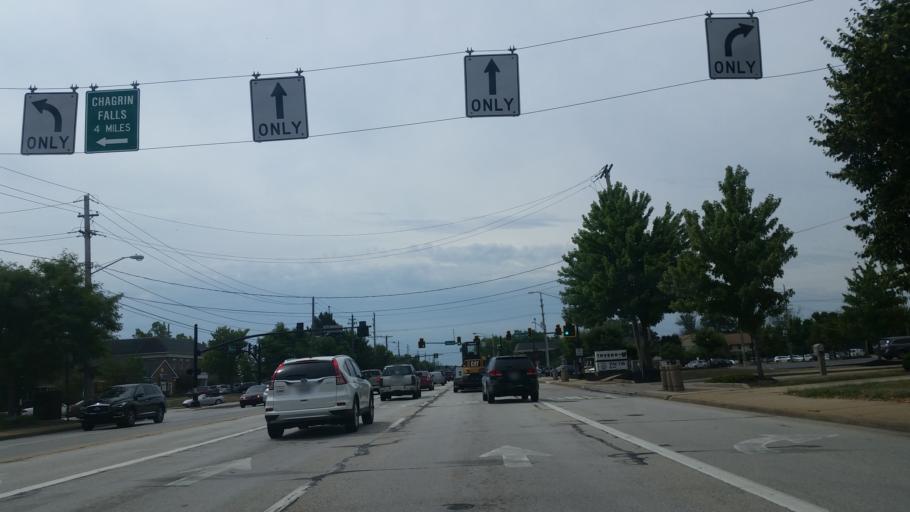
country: US
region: Ohio
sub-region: Cuyahoga County
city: Solon
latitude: 41.3928
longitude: -81.4378
